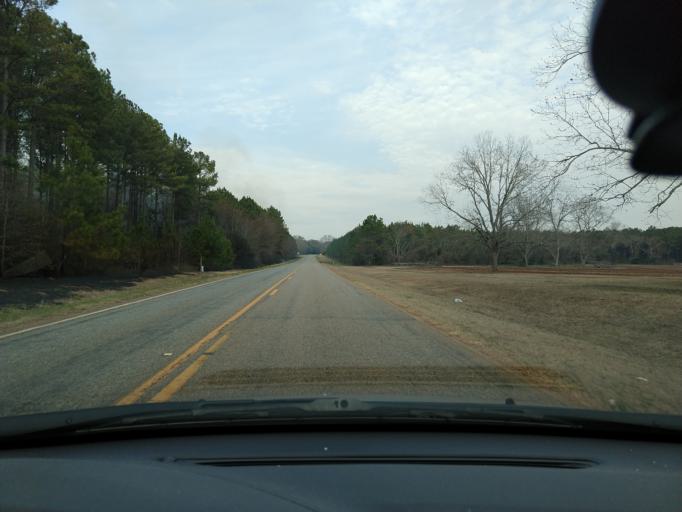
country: US
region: Georgia
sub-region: Webster County
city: Preston
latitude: 32.0169
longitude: -84.4056
